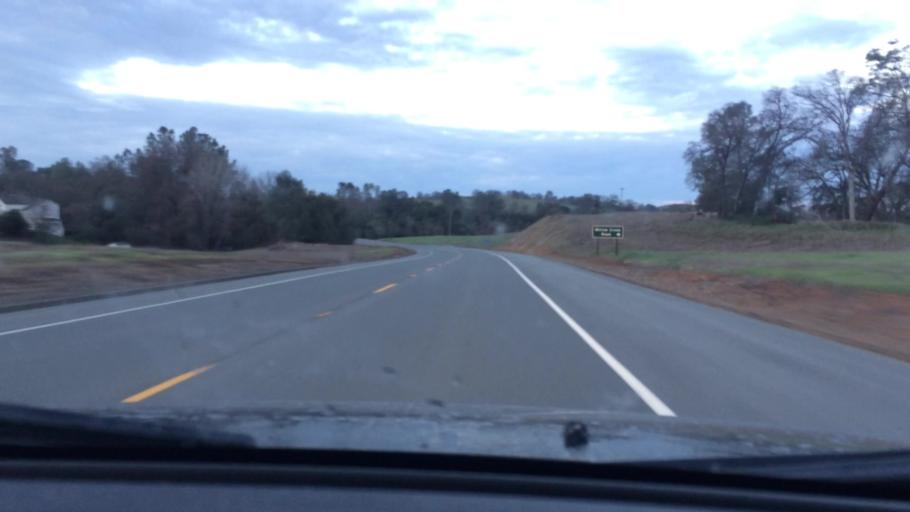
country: US
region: California
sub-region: Amador County
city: Ione
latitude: 38.3919
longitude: -120.9041
